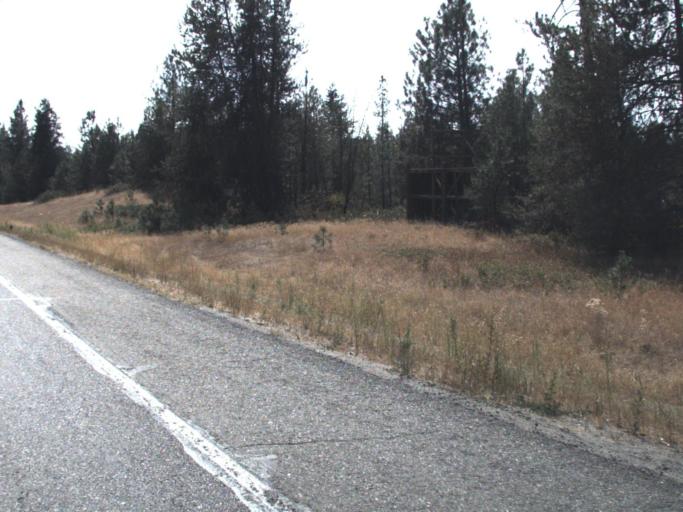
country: US
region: Washington
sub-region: Spokane County
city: Deer Park
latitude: 48.0685
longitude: -117.6247
